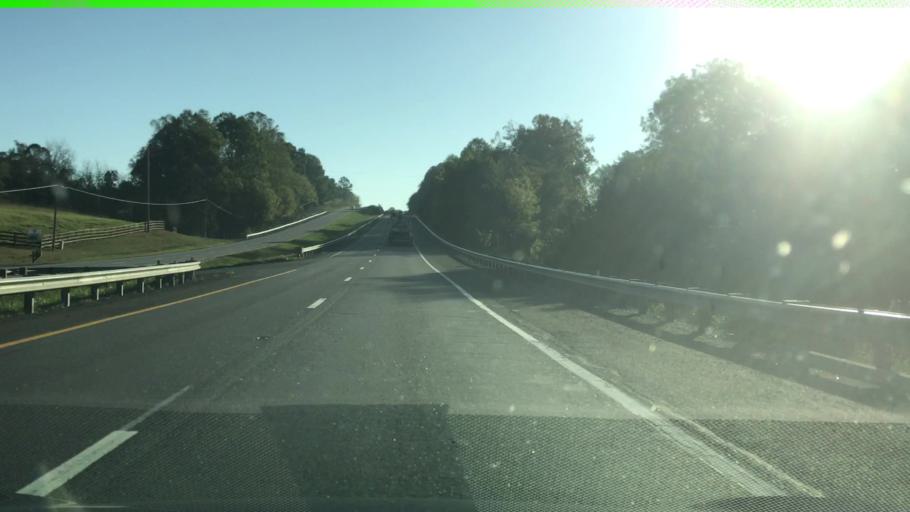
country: US
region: Virginia
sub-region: City of Bedford
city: Bedford
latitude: 37.3179
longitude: -79.4436
